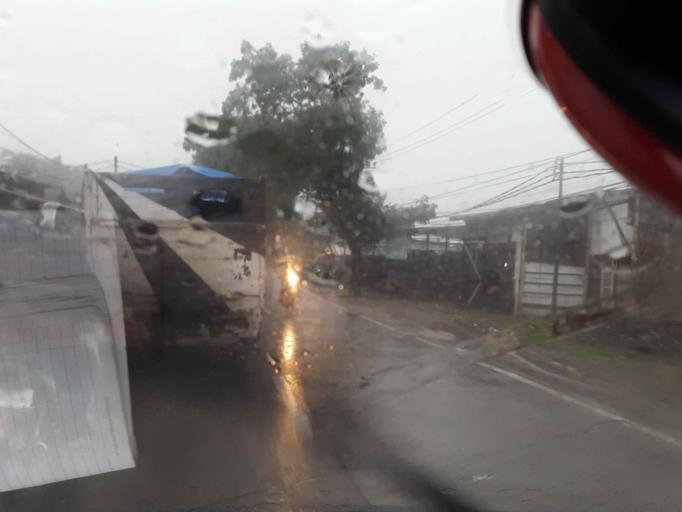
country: ID
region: West Java
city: Cimahi
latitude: -6.8753
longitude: 107.5040
